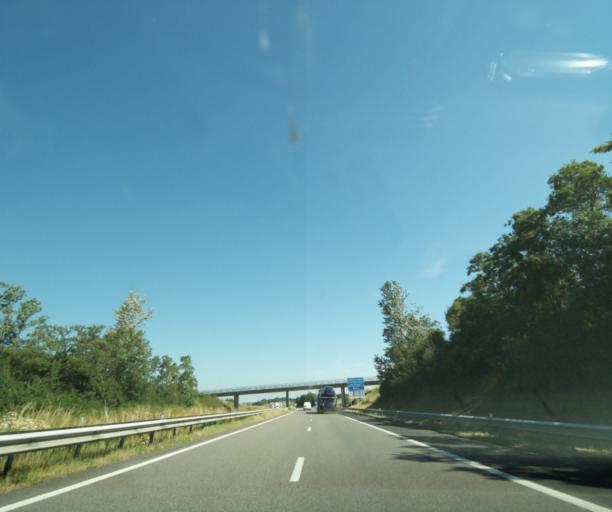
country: FR
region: Lorraine
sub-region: Departement des Vosges
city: Chatenois
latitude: 48.2574
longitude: 5.8653
